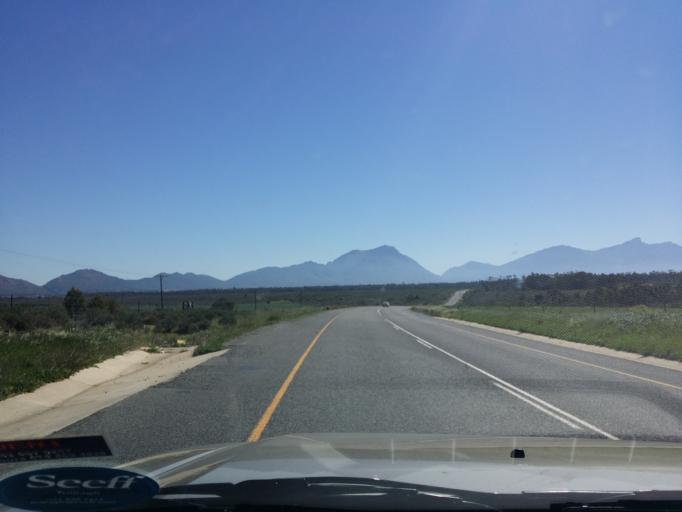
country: ZA
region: Western Cape
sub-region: Cape Winelands District Municipality
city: Ceres
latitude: -33.3624
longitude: 19.1693
